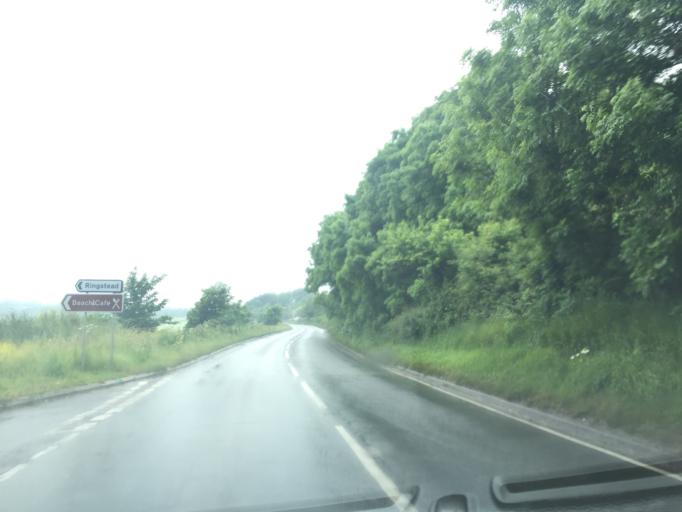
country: GB
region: England
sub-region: Dorset
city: Overcombe
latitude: 50.6498
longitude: -2.3692
